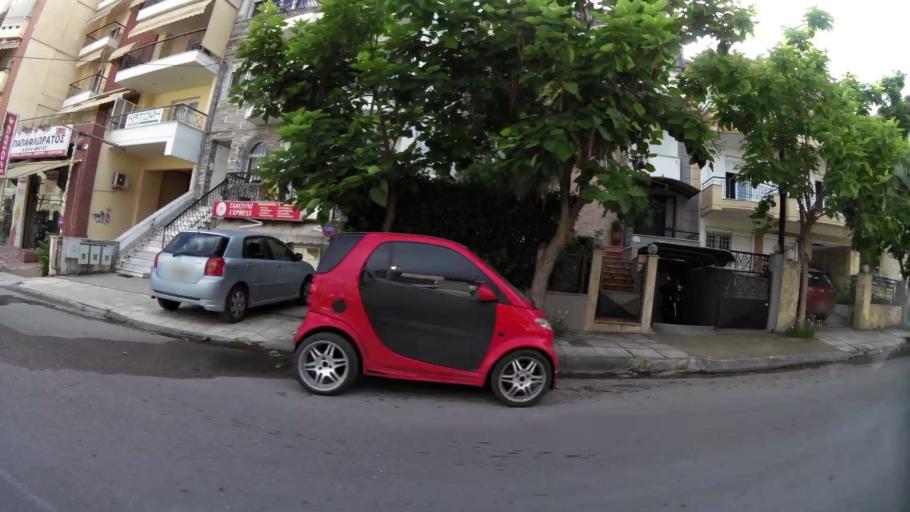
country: GR
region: Central Macedonia
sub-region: Nomos Thessalonikis
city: Kalamaria
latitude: 40.5726
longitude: 22.9692
